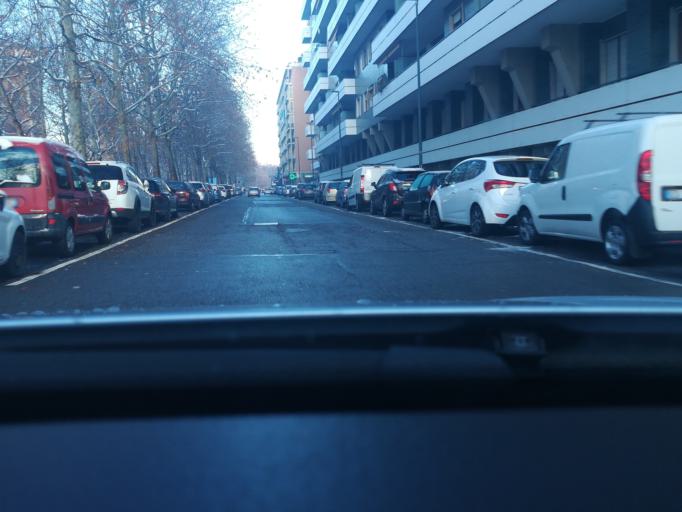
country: IT
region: Piedmont
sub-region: Provincia di Torino
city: Lesna
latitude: 45.0673
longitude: 7.6252
